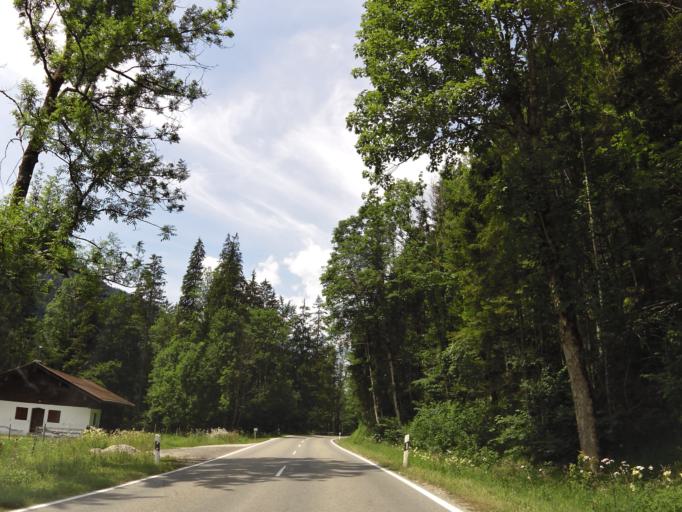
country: DE
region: Bavaria
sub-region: Upper Bavaria
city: Reit im Winkl
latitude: 47.6597
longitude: 12.5265
